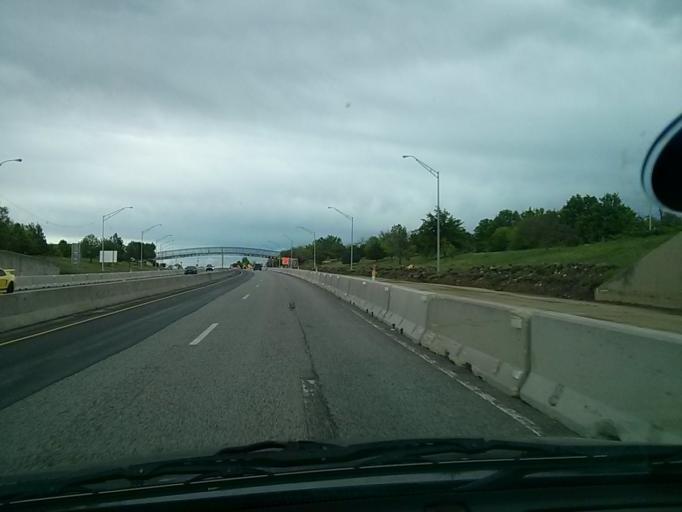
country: US
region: Oklahoma
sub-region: Tulsa County
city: Tulsa
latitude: 36.1605
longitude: -95.9573
